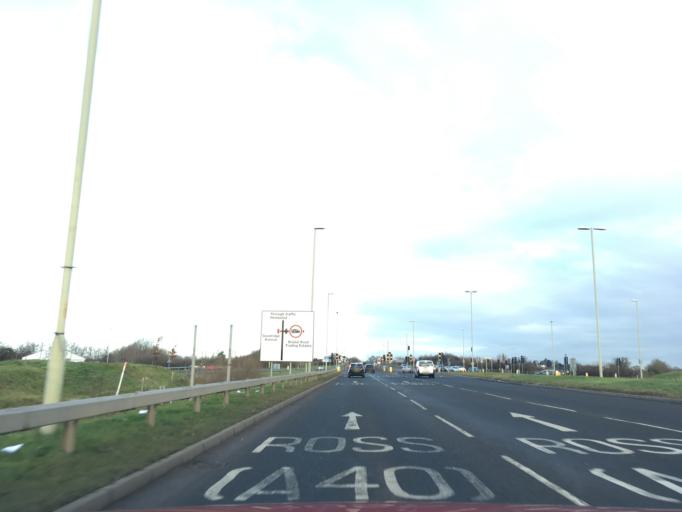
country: GB
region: England
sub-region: Gloucestershire
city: Gloucester
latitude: 51.8368
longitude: -2.2722
